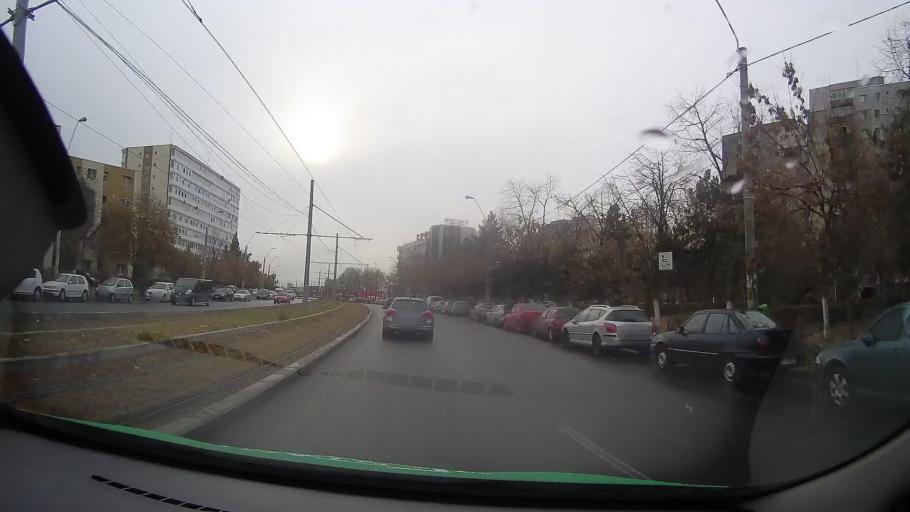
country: RO
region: Prahova
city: Ploiesti
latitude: 44.9300
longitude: 25.9898
